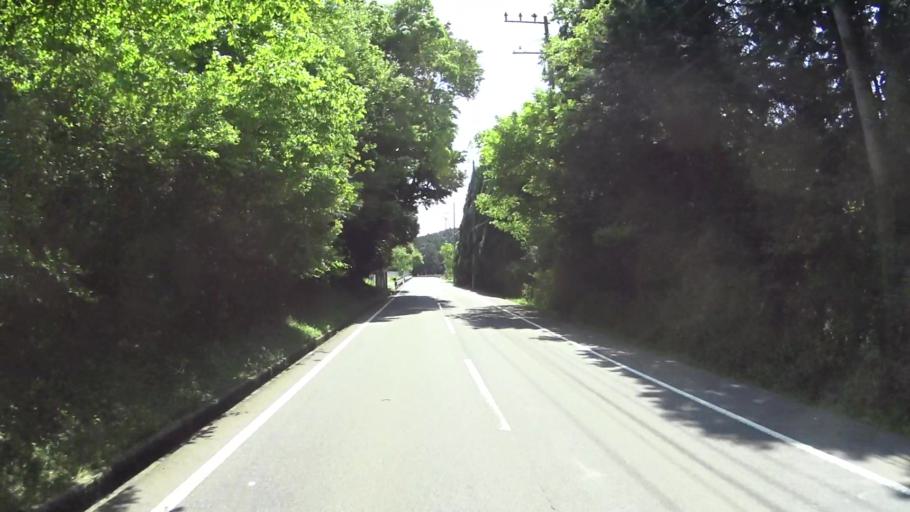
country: JP
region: Kyoto
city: Kameoka
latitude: 34.9987
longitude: 135.4788
